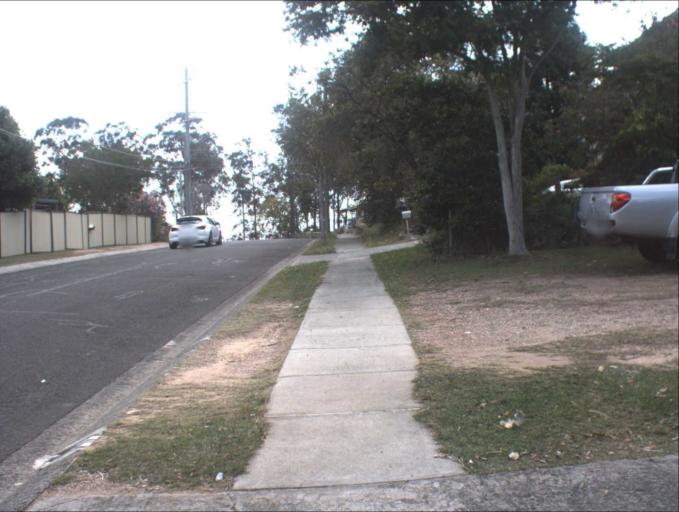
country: AU
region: Queensland
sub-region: Logan
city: Woodridge
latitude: -27.6207
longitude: 153.0983
